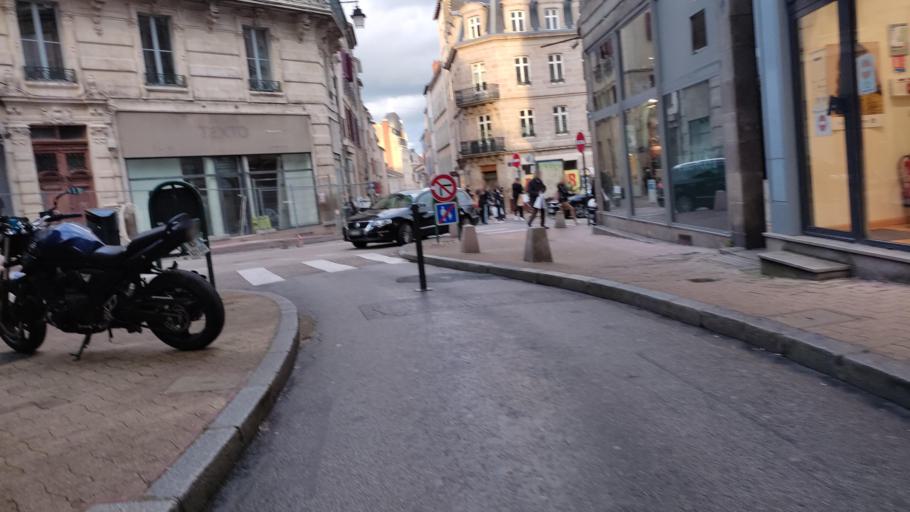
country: FR
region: Limousin
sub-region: Departement de la Haute-Vienne
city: Limoges
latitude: 45.8294
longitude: 1.2576
